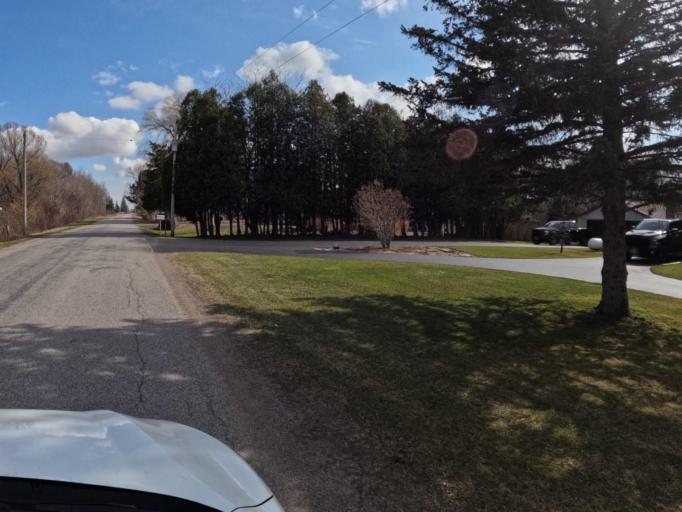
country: CA
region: Ontario
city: Norfolk County
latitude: 42.8906
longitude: -80.2854
